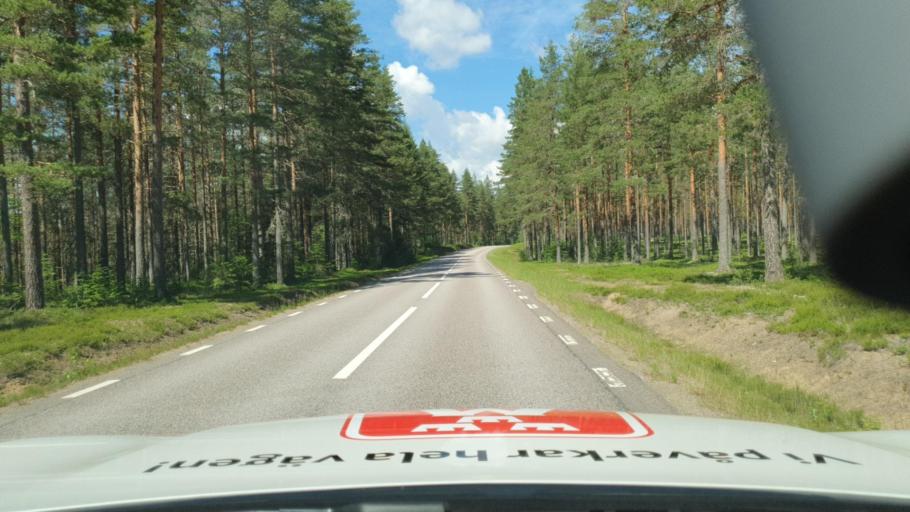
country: SE
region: Vaermland
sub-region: Torsby Kommun
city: Torsby
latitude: 60.3826
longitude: 12.9211
